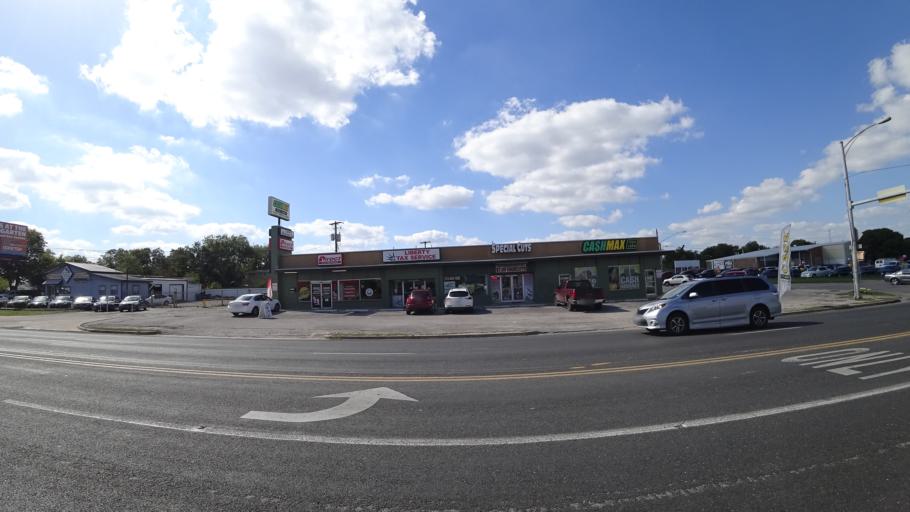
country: US
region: Texas
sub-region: Travis County
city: Austin
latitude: 30.3146
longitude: -97.7147
